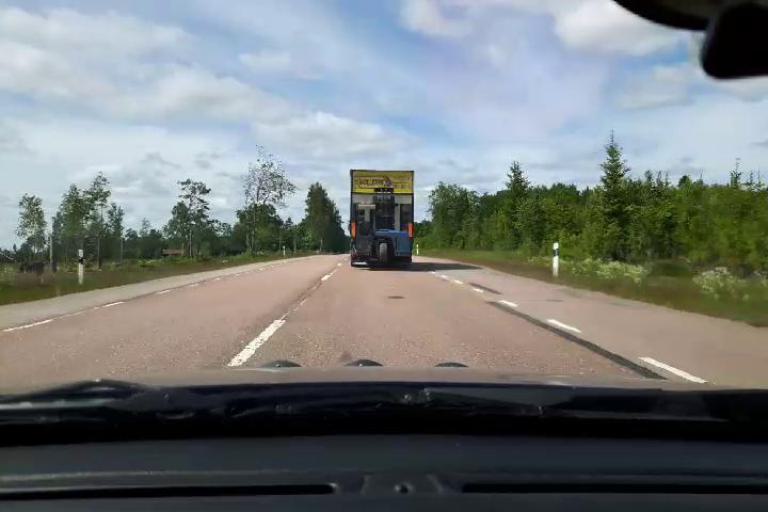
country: SE
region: Uppsala
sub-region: Osthammars Kommun
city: Bjorklinge
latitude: 60.1088
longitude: 17.5390
